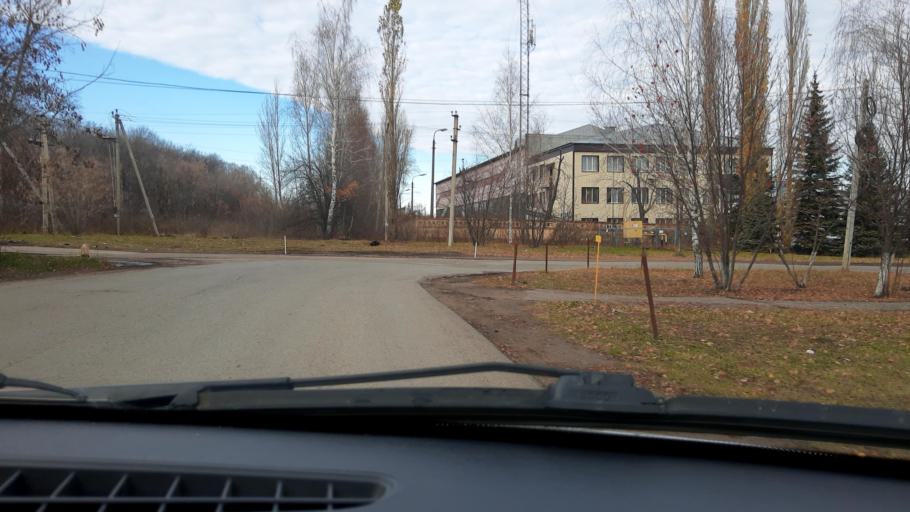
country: RU
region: Bashkortostan
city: Avdon
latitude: 54.6855
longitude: 55.7941
